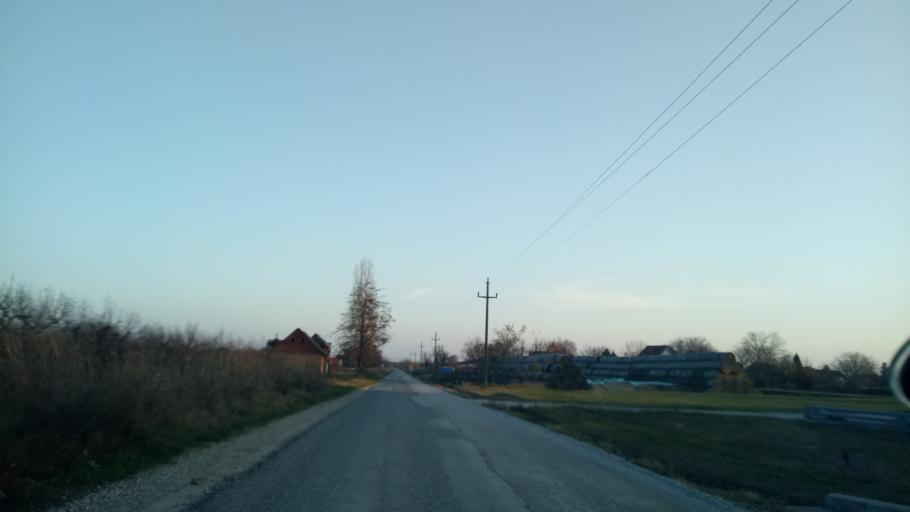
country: RS
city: Novi Slankamen
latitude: 45.1319
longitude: 20.2546
